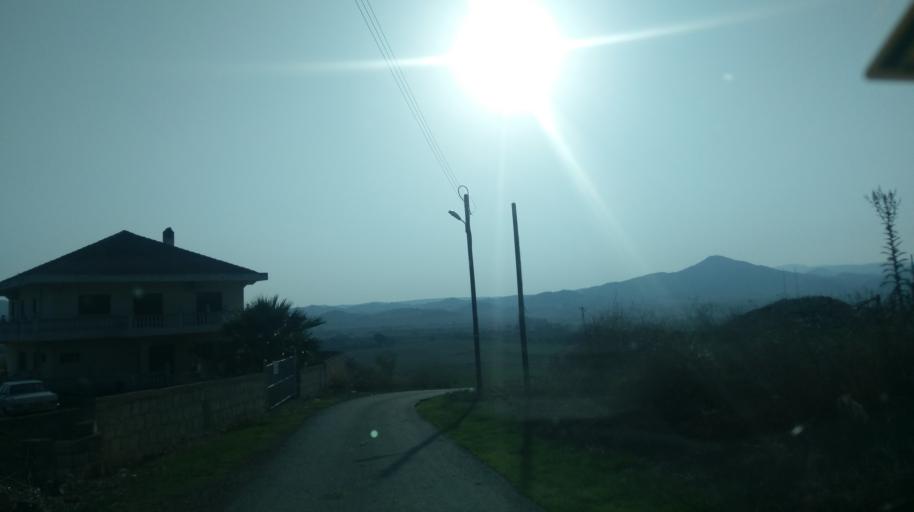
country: CY
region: Ammochostos
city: Leonarisso
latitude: 35.4765
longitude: 34.1041
